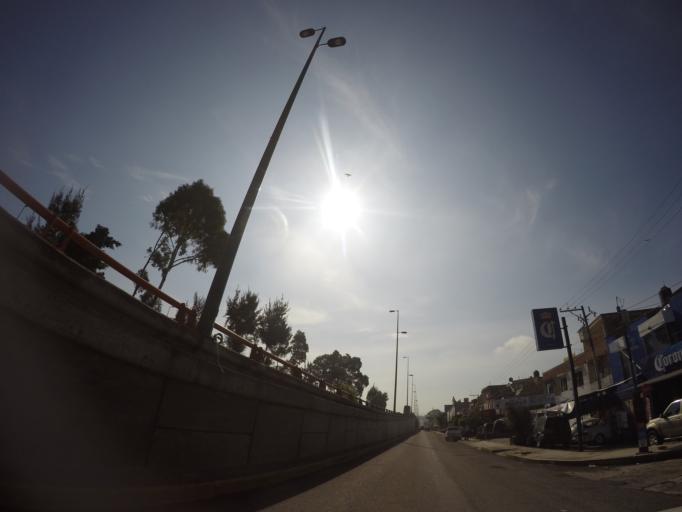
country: MX
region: Michoacan
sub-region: Tarimbaro
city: Real Hacienda (Metropolis)
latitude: 19.7257
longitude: -101.2076
